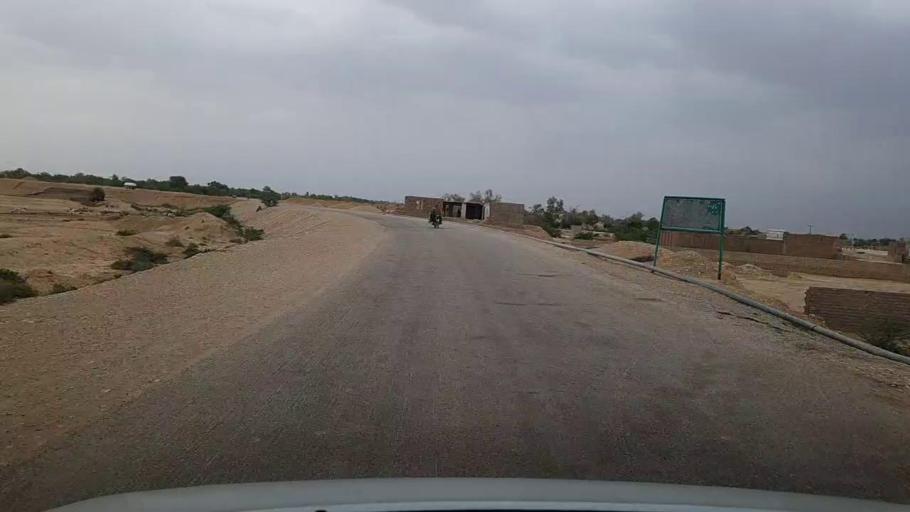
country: PK
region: Sindh
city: Sehwan
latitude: 26.3404
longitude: 67.7264
